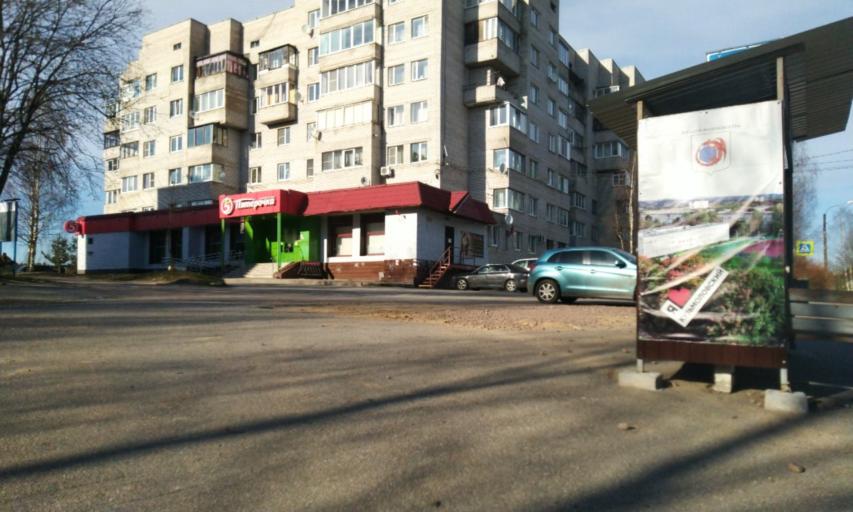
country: RU
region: Leningrad
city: Toksovo
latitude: 60.1197
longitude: 30.4989
